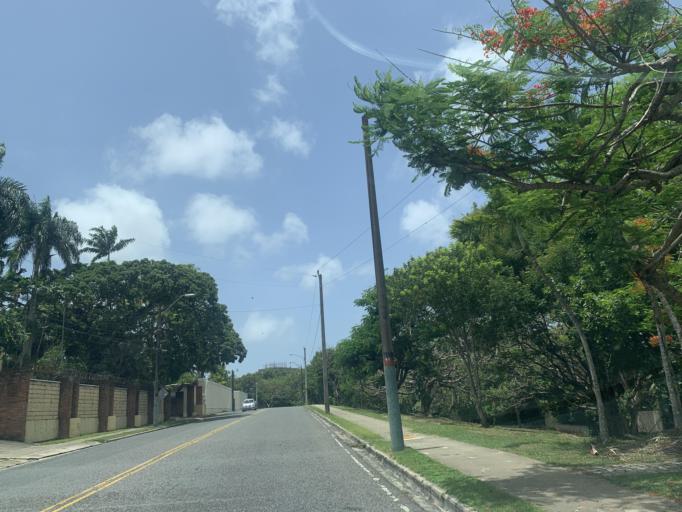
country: DO
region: Nacional
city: La Agustina
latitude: 18.4928
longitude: -69.9485
